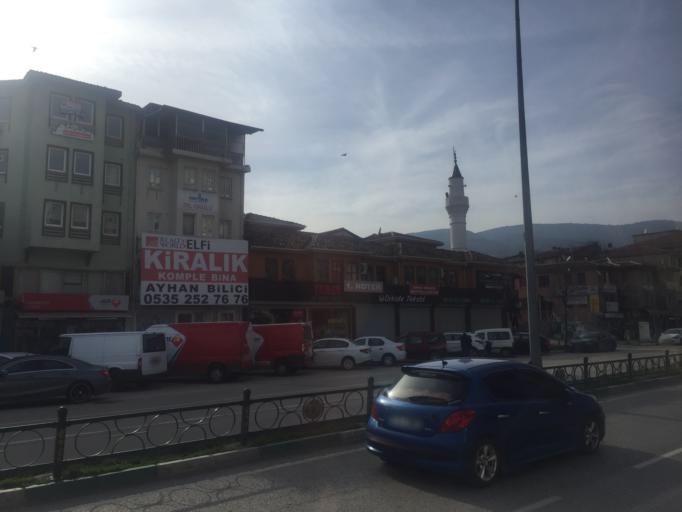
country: TR
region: Bursa
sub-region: Osmangazi
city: Bursa
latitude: 40.1881
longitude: 29.0646
